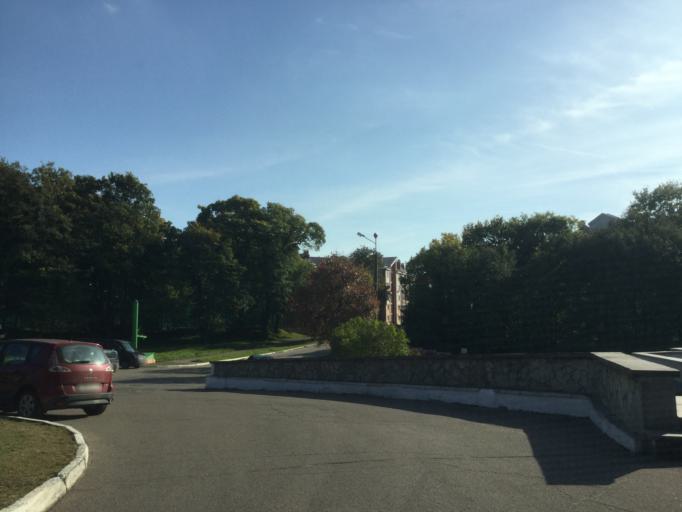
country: BY
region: Vitebsk
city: Vitebsk
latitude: 55.1745
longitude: 30.1954
